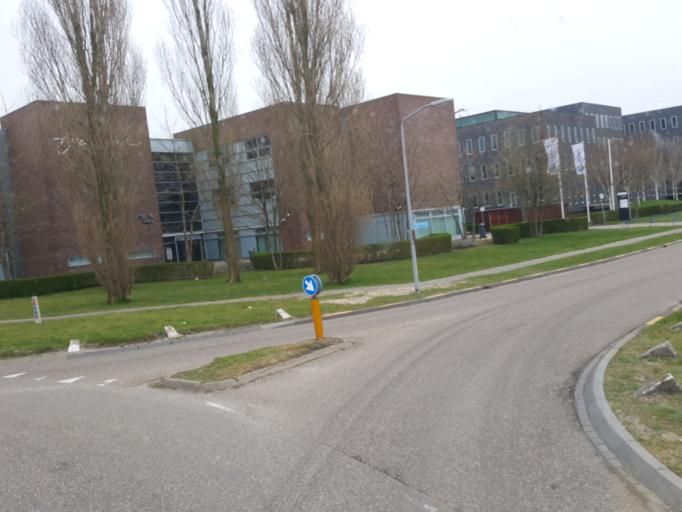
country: NL
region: Flevoland
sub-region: Gemeente Almere
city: Almere Stad
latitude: 52.3496
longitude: 5.1773
